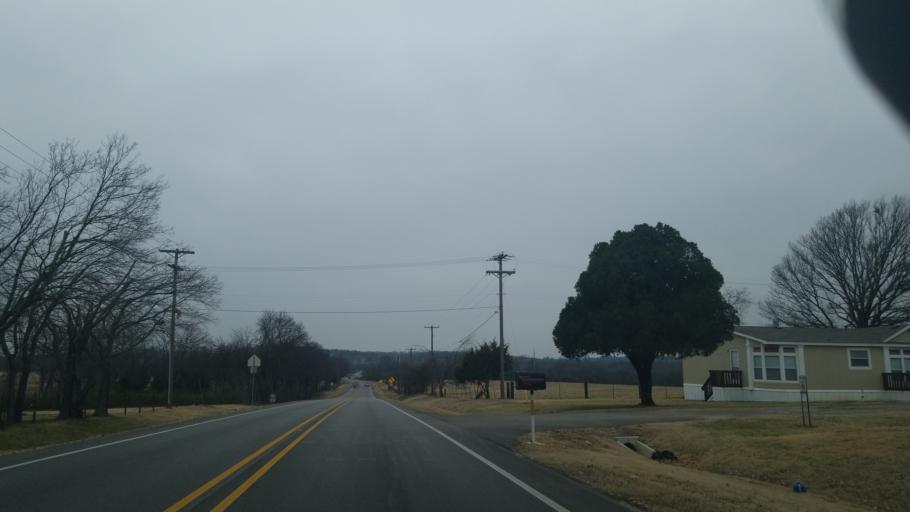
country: US
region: Texas
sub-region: Denton County
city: Argyle
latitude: 33.1576
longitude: -97.1420
